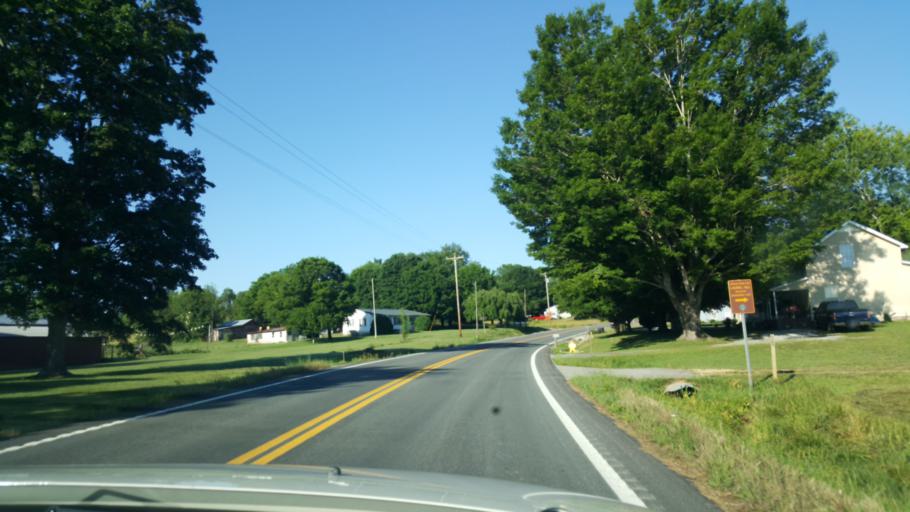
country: US
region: Tennessee
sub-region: Lawrence County
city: Lawrenceburg
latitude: 35.3934
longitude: -87.3916
